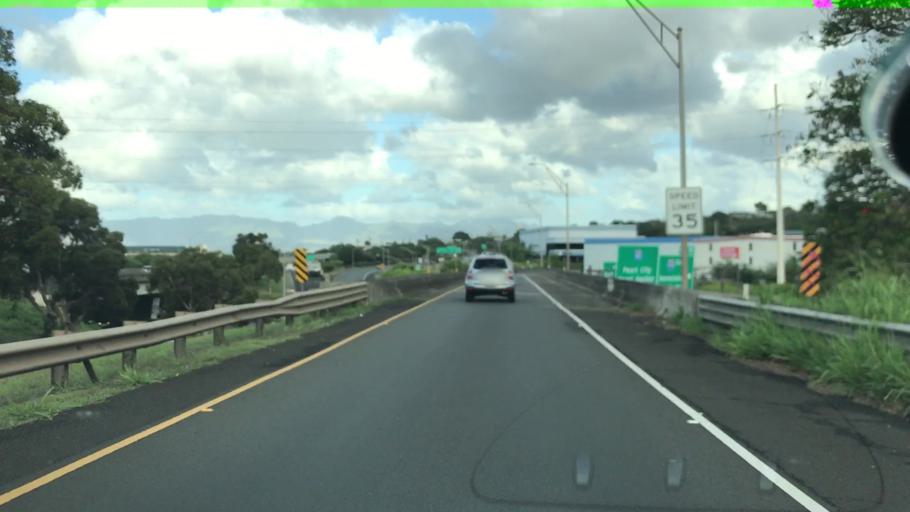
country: US
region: Hawaii
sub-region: Honolulu County
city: Halawa Heights
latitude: 21.3702
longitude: -157.9130
